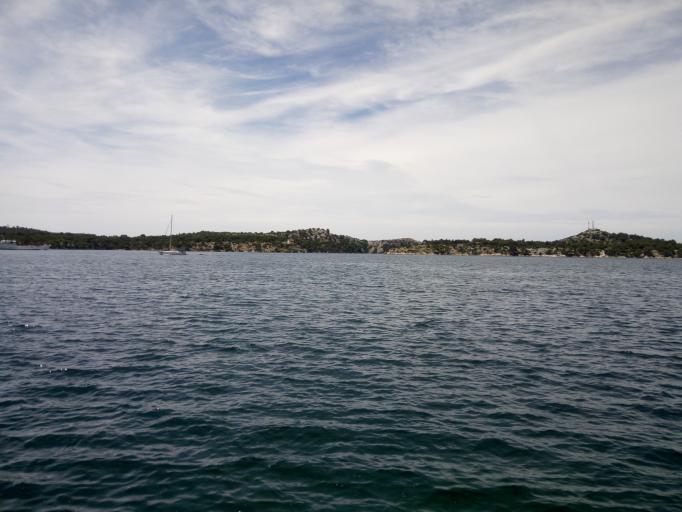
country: HR
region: Sibensko-Kniniska
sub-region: Grad Sibenik
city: Sibenik
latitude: 43.7350
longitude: 15.8886
